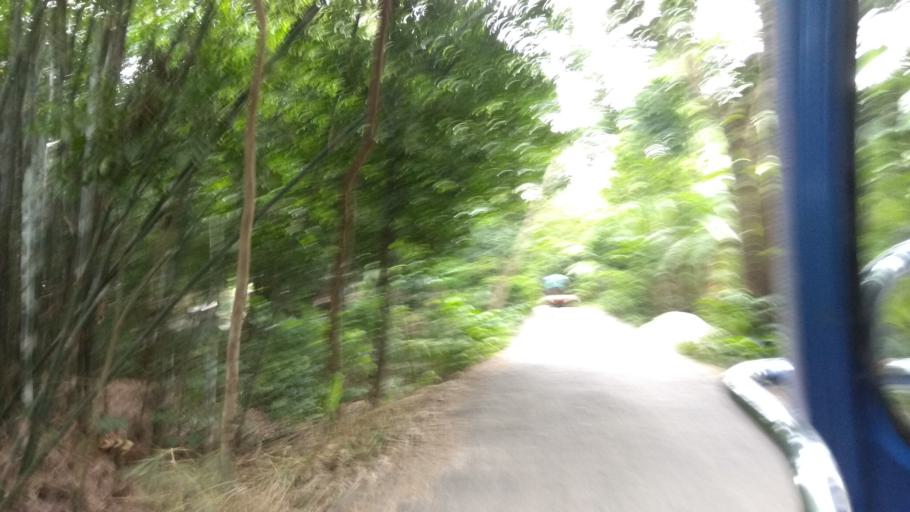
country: BD
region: Khulna
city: Kalia
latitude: 23.0330
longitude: 89.6557
